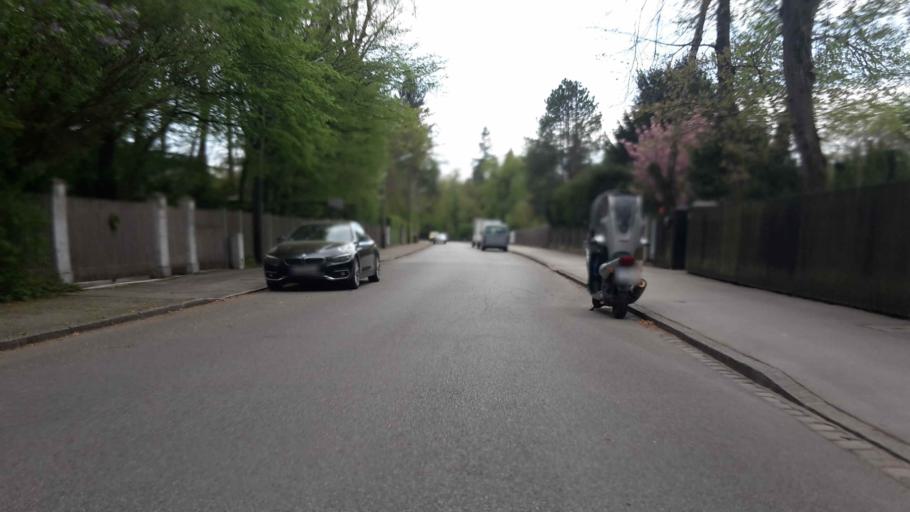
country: DE
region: Bavaria
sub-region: Upper Bavaria
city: Pasing
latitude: 48.1741
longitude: 11.4885
